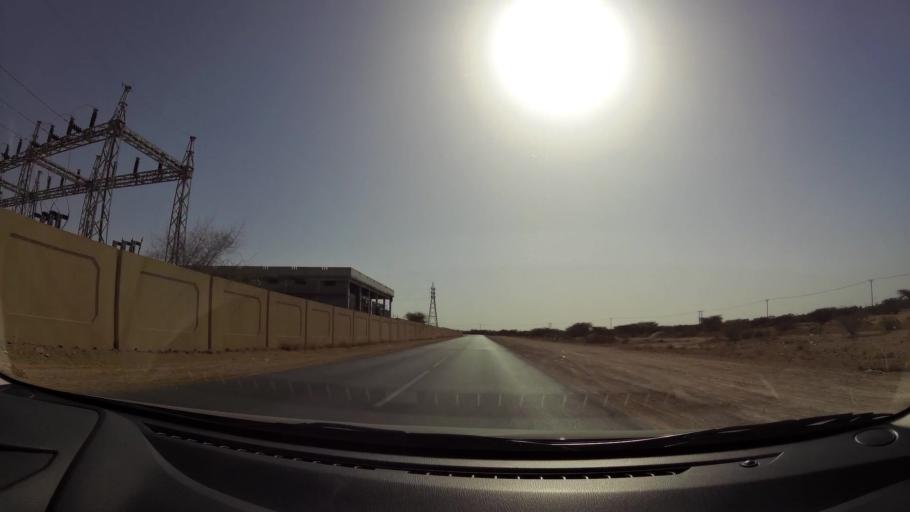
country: OM
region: Muhafazat Masqat
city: As Sib al Jadidah
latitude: 23.5851
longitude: 58.2461
